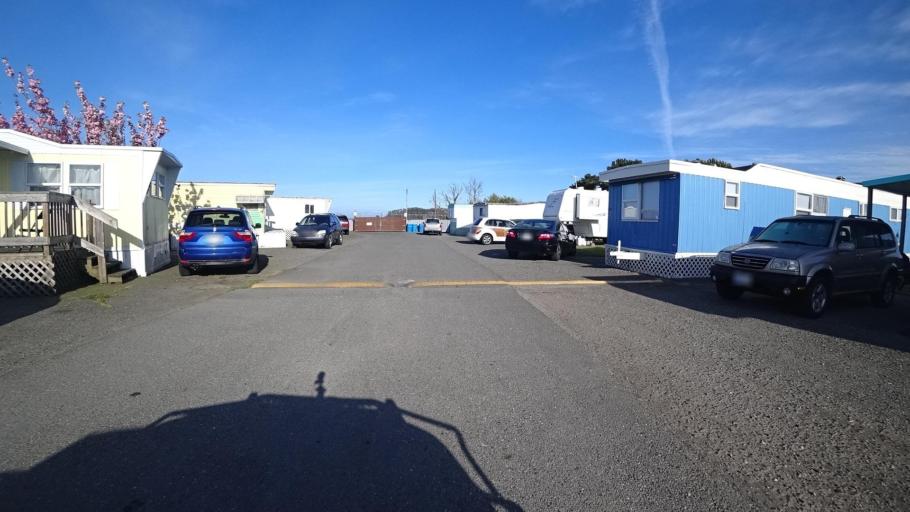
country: US
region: California
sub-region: Humboldt County
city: Bayview
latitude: 40.7746
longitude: -124.1933
